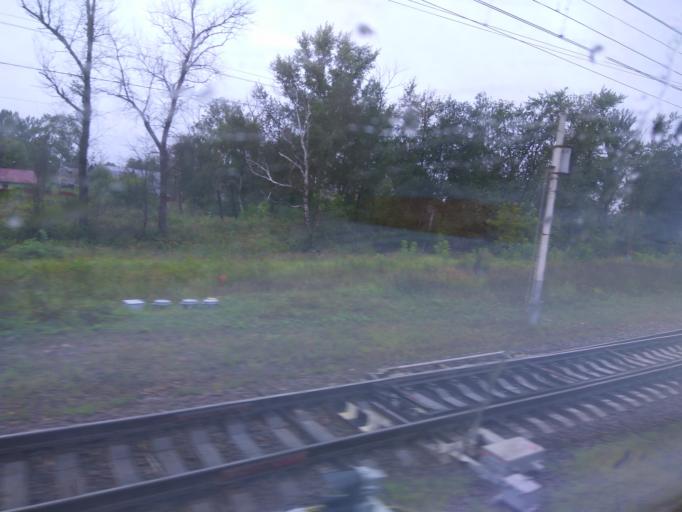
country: RU
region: Moskovskaya
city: Zhilevo
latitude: 54.9835
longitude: 38.0326
